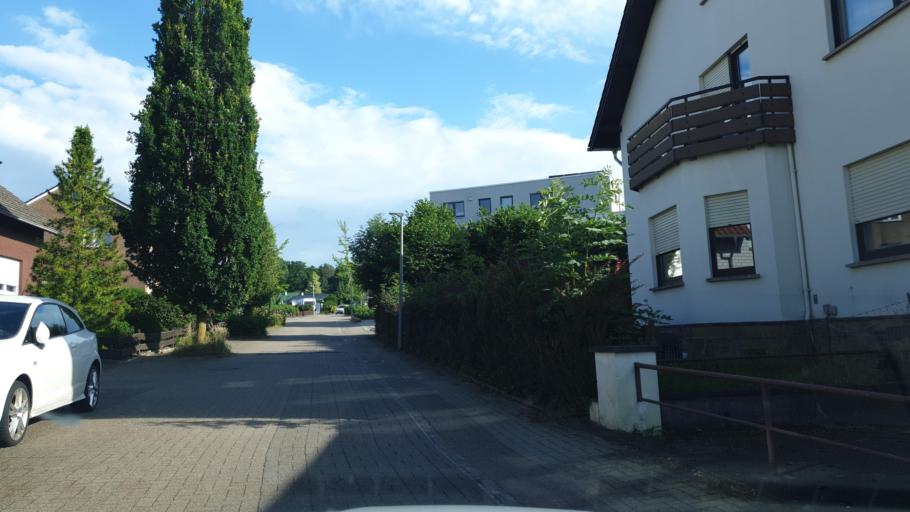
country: DE
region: North Rhine-Westphalia
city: Bad Oeynhausen
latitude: 52.1886
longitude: 8.7923
